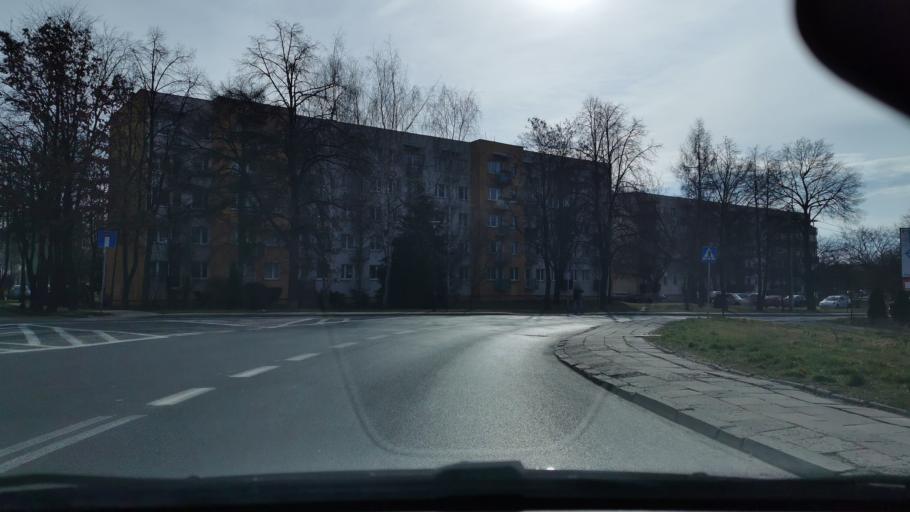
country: PL
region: Lublin Voivodeship
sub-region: Powiat lubelski
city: Lublin
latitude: 51.2050
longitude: 22.5433
